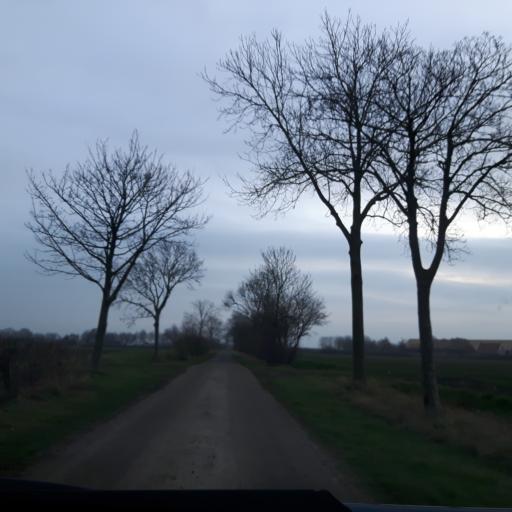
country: NL
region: Zeeland
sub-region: Gemeente Terneuzen
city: Terneuzen
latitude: 51.3990
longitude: 3.8446
